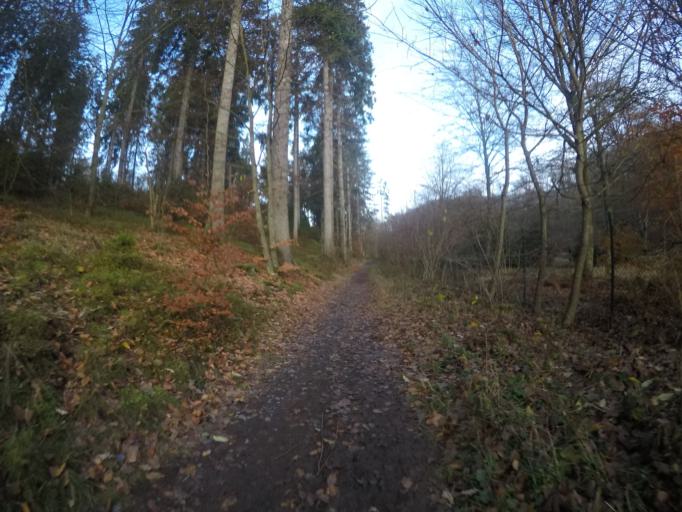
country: BE
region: Wallonia
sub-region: Province du Luxembourg
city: Habay-la-Vieille
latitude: 49.7423
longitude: 5.6729
